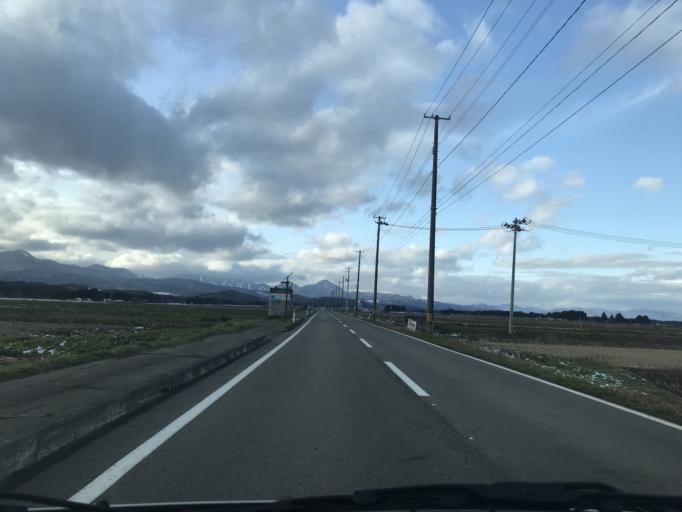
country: JP
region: Iwate
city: Mizusawa
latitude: 39.1991
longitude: 141.0639
